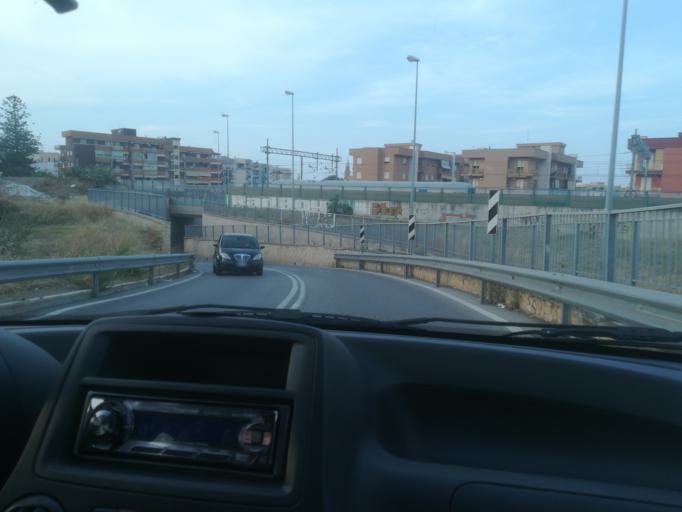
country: IT
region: Apulia
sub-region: Provincia di Bari
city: Monopoli
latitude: 40.9450
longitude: 17.3020
